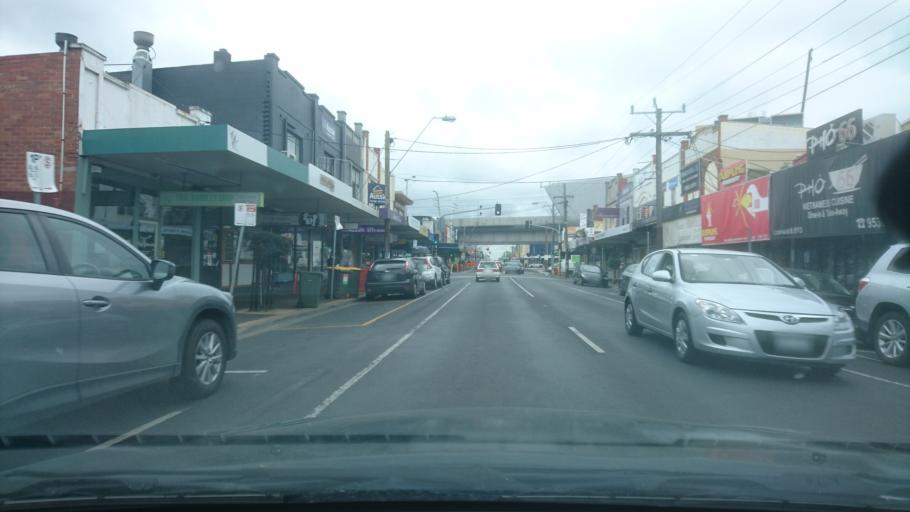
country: AU
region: Victoria
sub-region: Glen Eira
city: Carnegie
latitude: -37.8870
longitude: 145.0575
